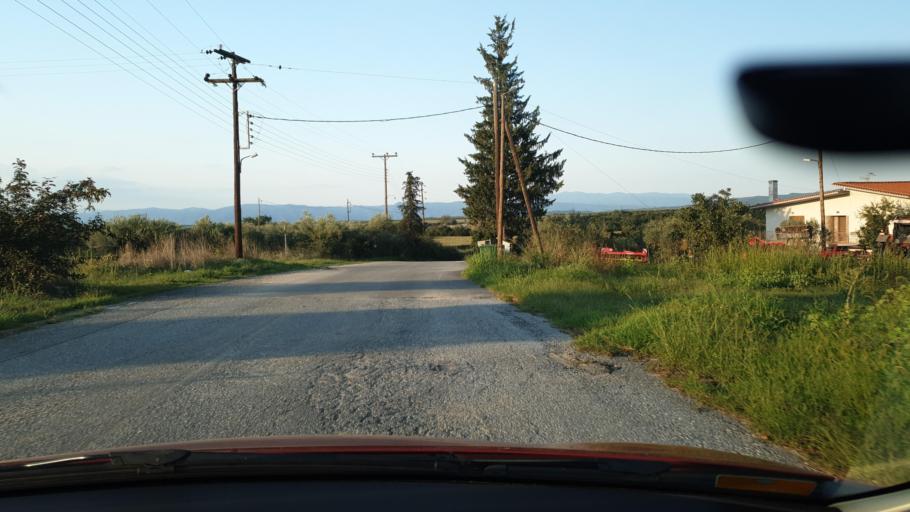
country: GR
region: Central Macedonia
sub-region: Nomos Thessalonikis
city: Nea Apollonia
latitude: 40.5490
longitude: 23.4492
